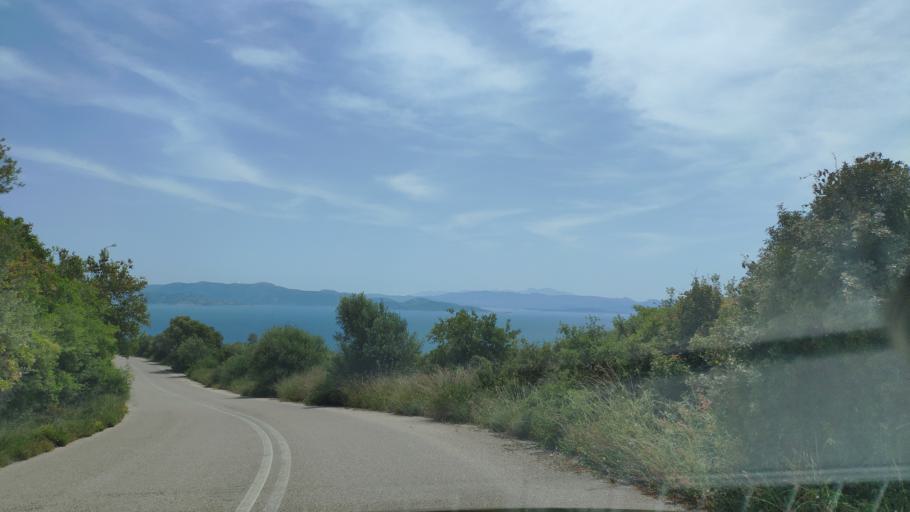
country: GR
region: Attica
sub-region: Nomarchia Anatolikis Attikis
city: Grammatiko
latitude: 38.2571
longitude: 23.9720
